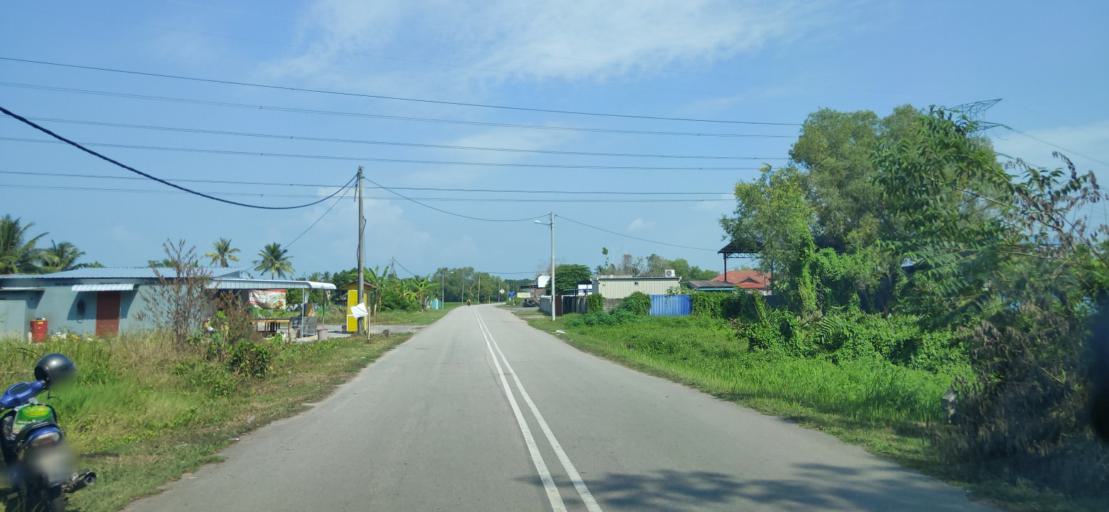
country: MY
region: Kedah
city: Sungai Petani
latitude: 5.6748
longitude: 100.4663
